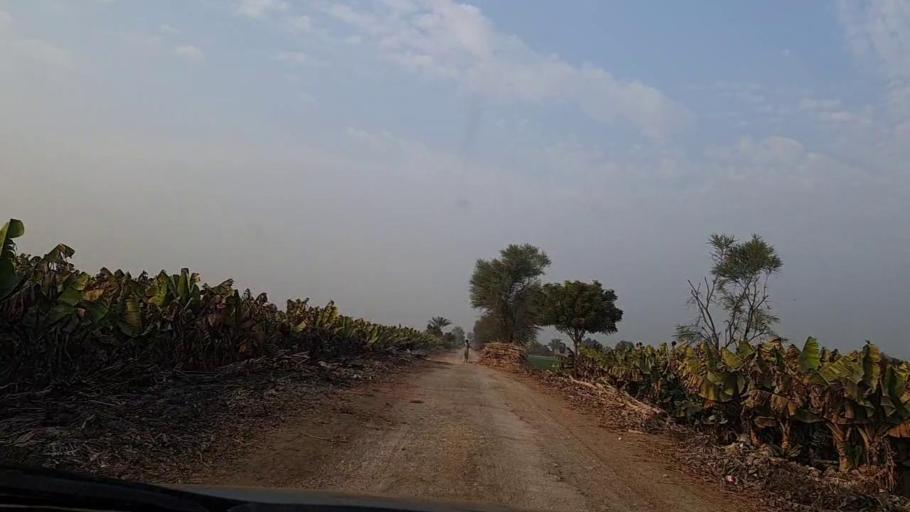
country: PK
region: Sindh
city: Nawabshah
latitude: 26.2904
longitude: 68.2854
